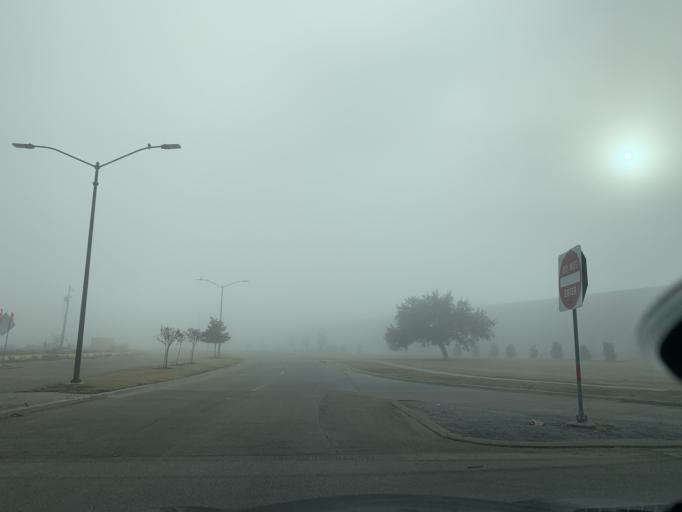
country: US
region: Texas
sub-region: Tarrant County
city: Euless
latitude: 32.8323
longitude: -97.0603
